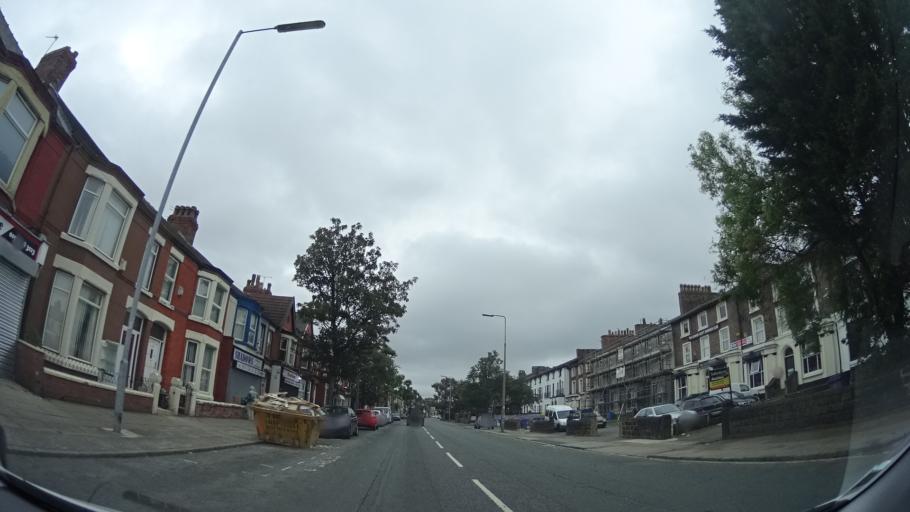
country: GB
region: England
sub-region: Liverpool
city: Liverpool
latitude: 53.4163
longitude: -2.9146
